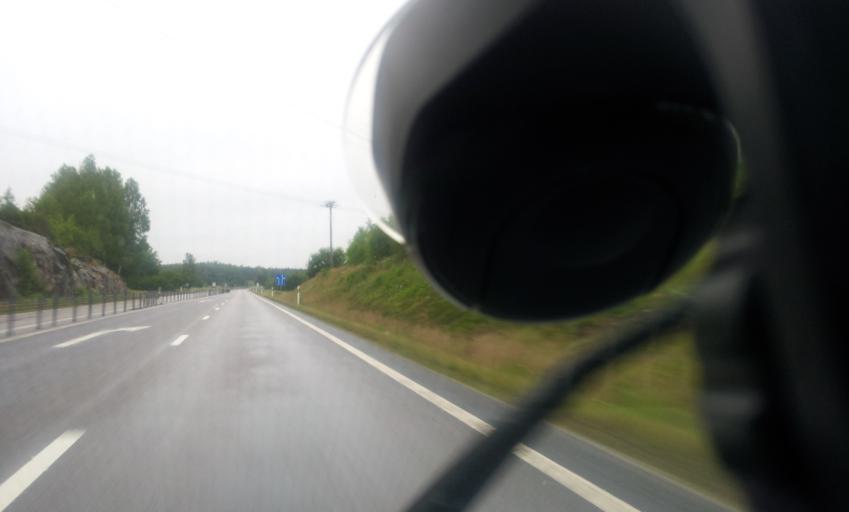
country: SE
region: OEstergoetland
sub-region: Valdemarsviks Kommun
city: Valdemarsvik
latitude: 58.1170
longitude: 16.5399
